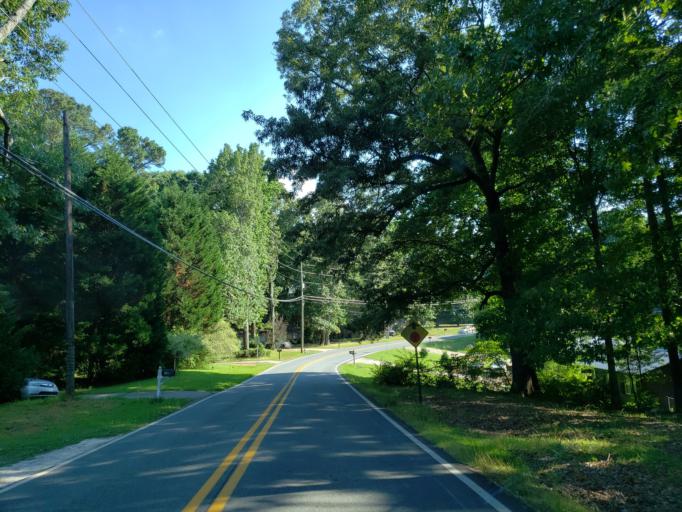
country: US
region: Georgia
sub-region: Cherokee County
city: Woodstock
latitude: 34.0932
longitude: -84.5438
